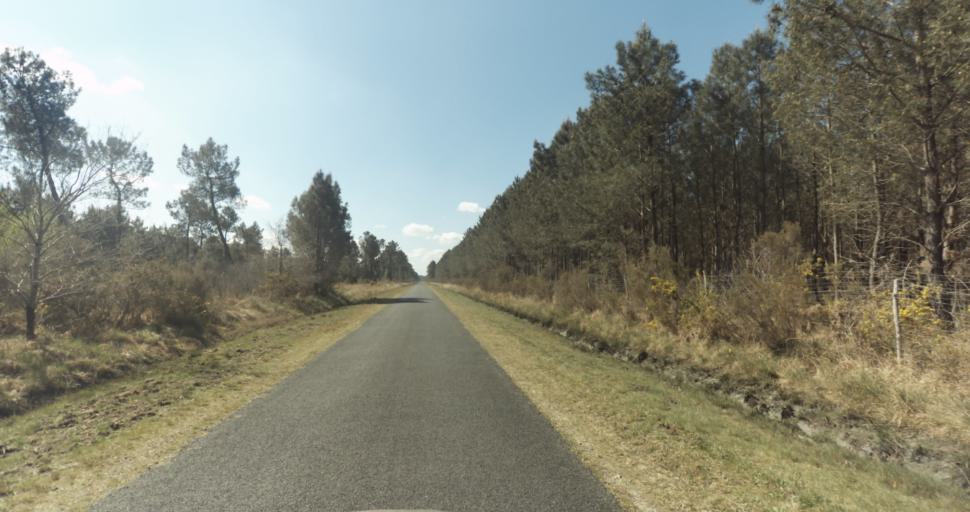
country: FR
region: Aquitaine
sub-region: Departement de la Gironde
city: Martignas-sur-Jalle
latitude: 44.7863
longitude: -0.7992
